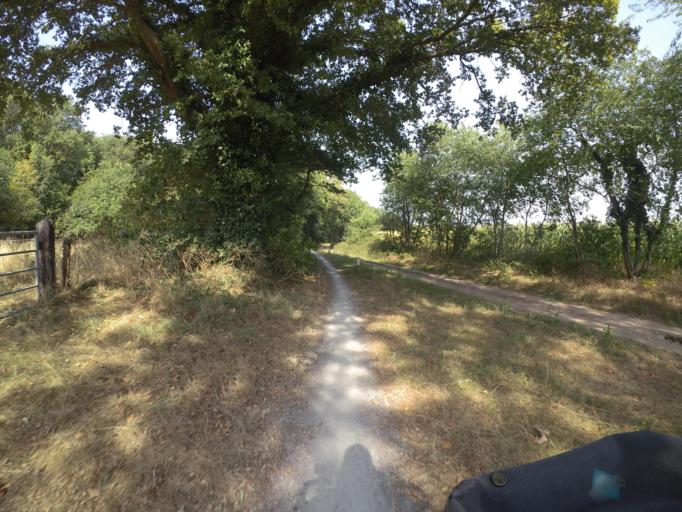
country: NL
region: Drenthe
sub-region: Gemeente Westerveld
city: Havelte
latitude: 52.7822
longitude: 6.2138
